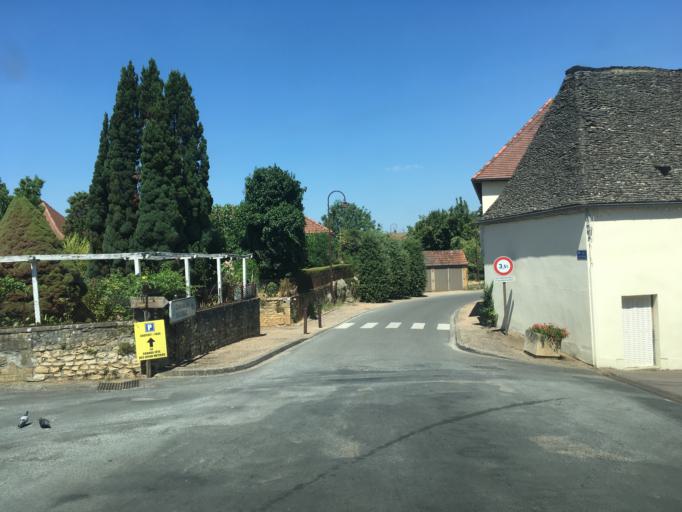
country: FR
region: Aquitaine
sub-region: Departement de la Dordogne
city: Eyvigues-et-Eybenes
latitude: 44.9743
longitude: 1.3226
